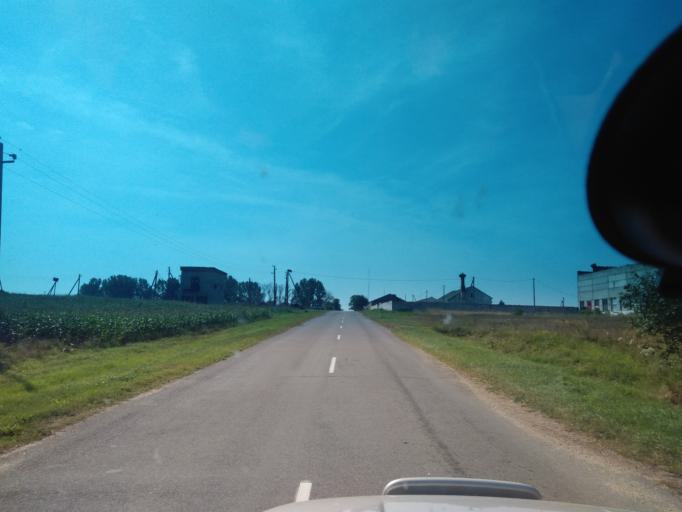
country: BY
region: Minsk
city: Kapyl'
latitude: 53.2113
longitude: 27.1248
